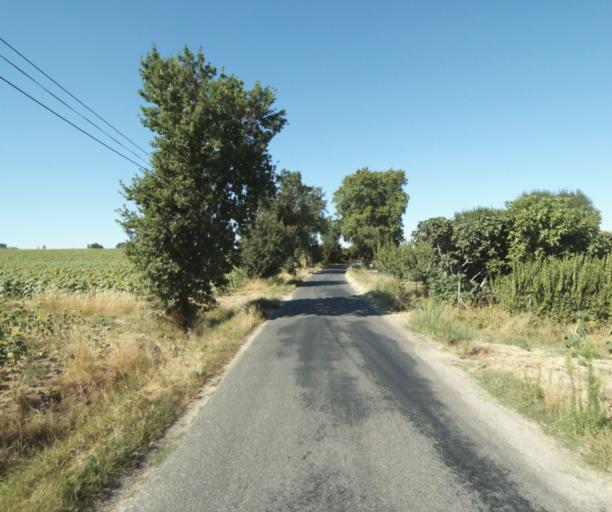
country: FR
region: Midi-Pyrenees
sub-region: Departement de la Haute-Garonne
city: Revel
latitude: 43.5004
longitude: 1.9454
